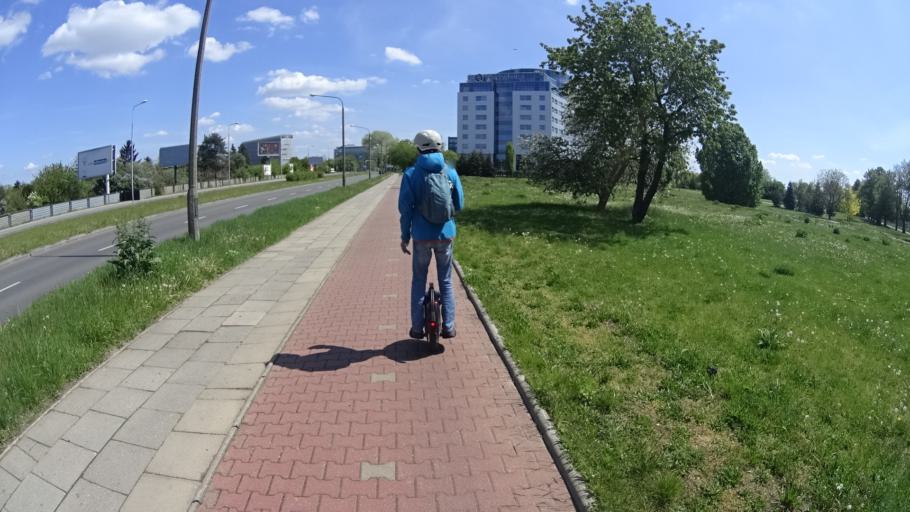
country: PL
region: Masovian Voivodeship
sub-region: Warszawa
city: Wlochy
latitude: 52.1840
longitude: 20.9616
